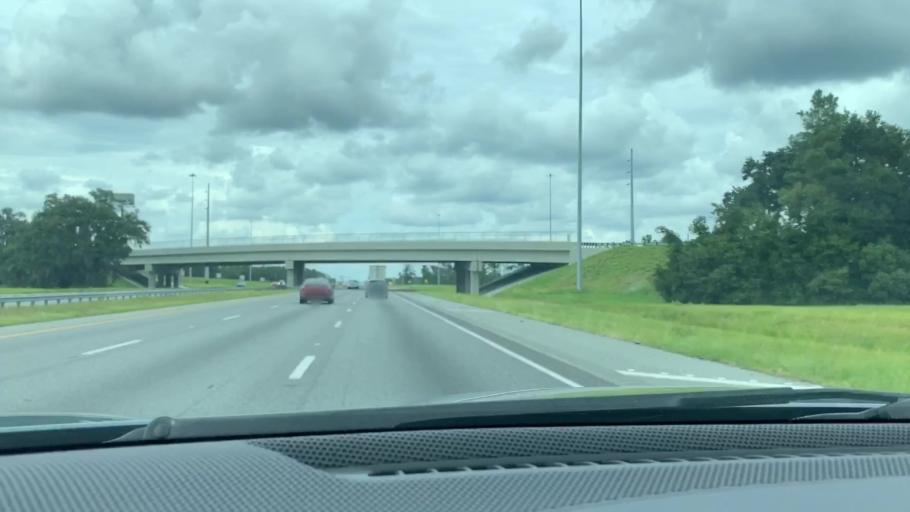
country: US
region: Georgia
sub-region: McIntosh County
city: Darien
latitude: 31.3950
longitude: -81.4486
